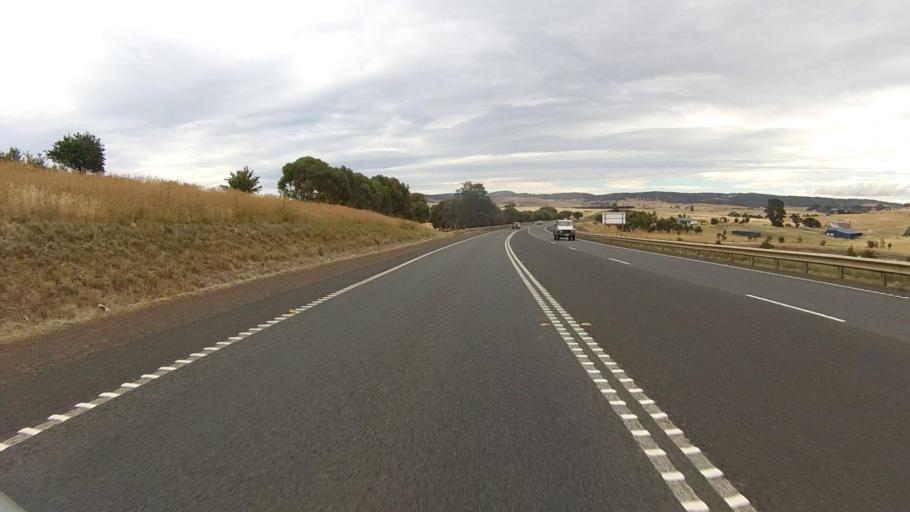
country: AU
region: Tasmania
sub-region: Brighton
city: Bridgewater
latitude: -42.3285
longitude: 147.3434
